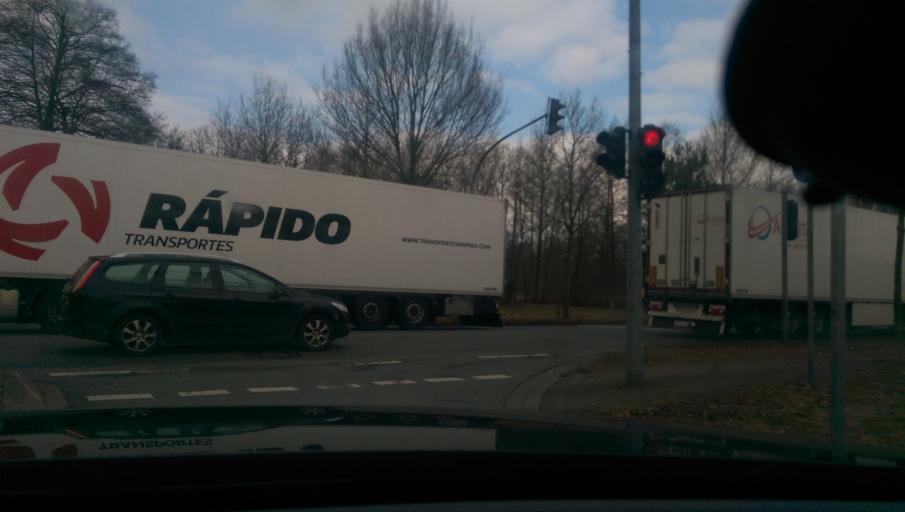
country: DE
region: Lower Saxony
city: Verden
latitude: 52.9139
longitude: 9.2697
